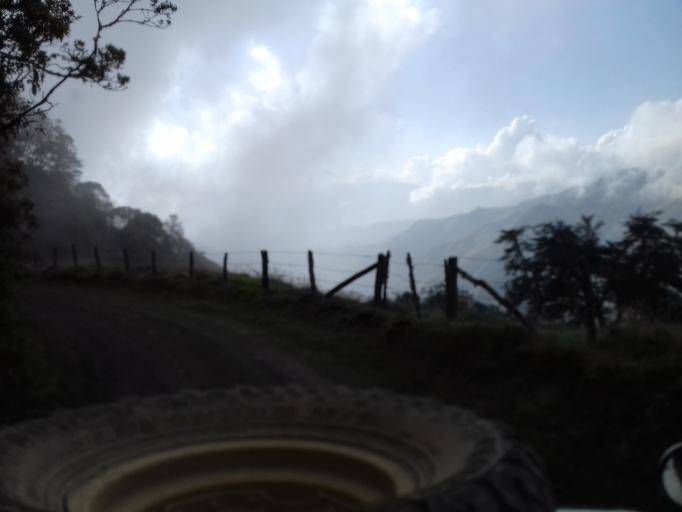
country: CO
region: Quindio
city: Salento
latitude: 4.5549
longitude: -75.5033
